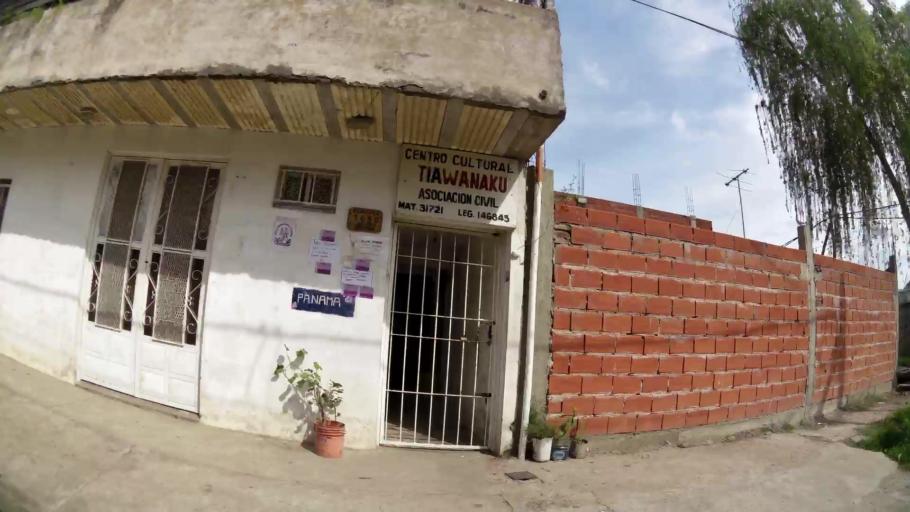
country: AR
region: Buenos Aires
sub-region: Partido de Quilmes
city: Quilmes
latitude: -34.7586
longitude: -58.2533
